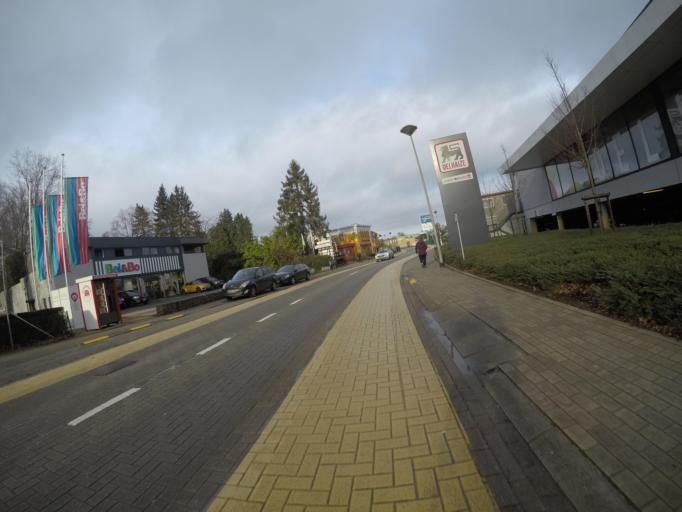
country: BE
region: Flanders
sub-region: Provincie Vlaams-Brabant
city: Liedekerke
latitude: 50.8721
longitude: 4.0802
